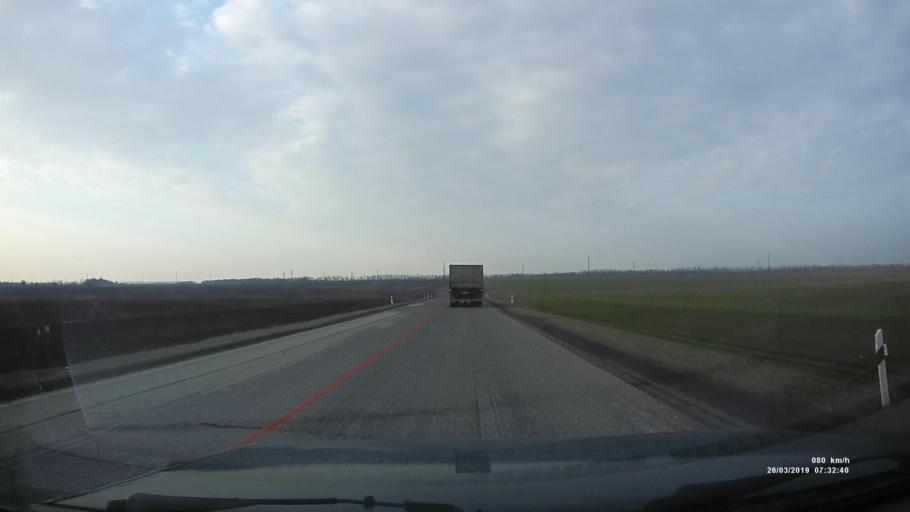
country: RU
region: Rostov
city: Novobessergenovka
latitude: 47.2233
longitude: 38.7760
